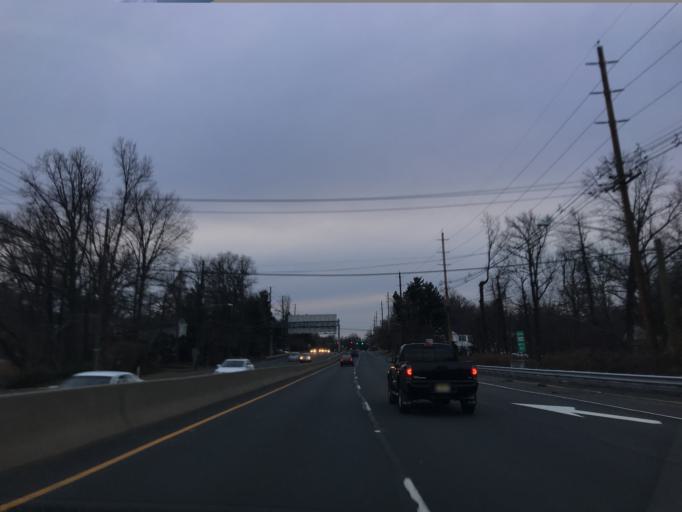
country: US
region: New Jersey
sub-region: Middlesex County
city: Milltown
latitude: 40.4571
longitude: -74.4562
